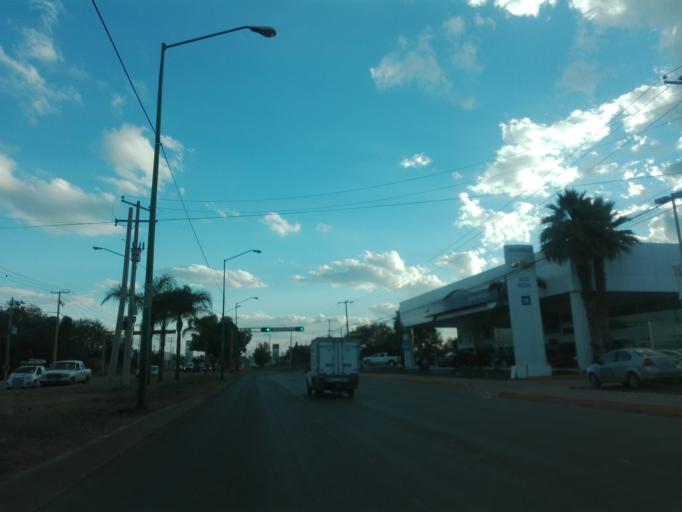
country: MX
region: Guanajuato
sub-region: Leon
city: San Jose de Duran (Los Troncoso)
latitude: 21.0877
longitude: -101.6795
